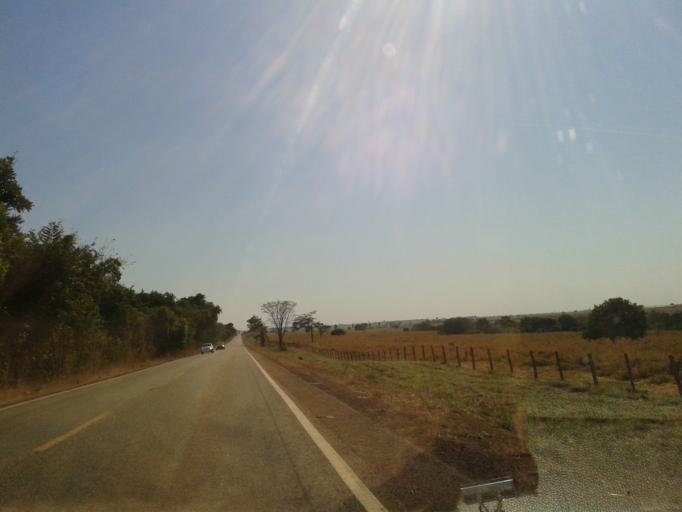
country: BR
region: Goias
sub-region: Mozarlandia
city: Mozarlandia
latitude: -14.3804
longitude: -50.4344
